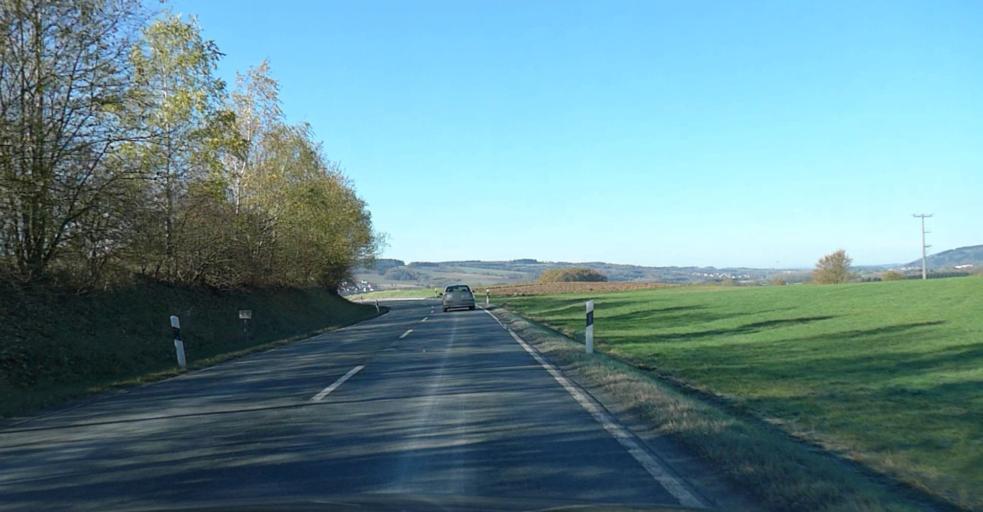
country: DE
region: Bavaria
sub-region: Upper Franconia
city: Kupferberg
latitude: 50.1299
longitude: 11.5552
